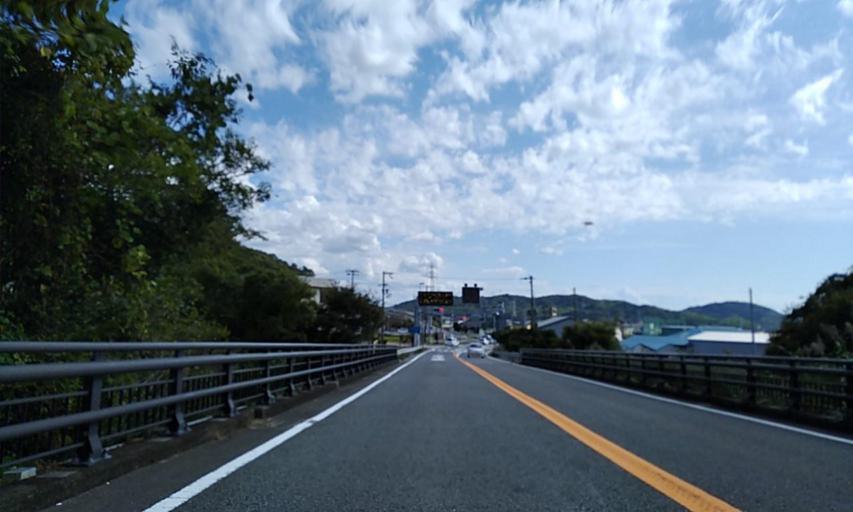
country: JP
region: Wakayama
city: Gobo
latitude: 33.9329
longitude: 135.1404
